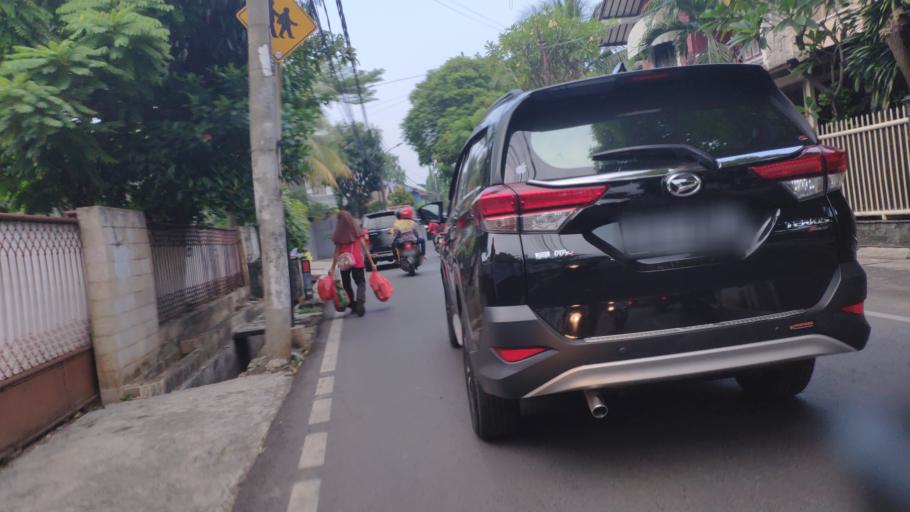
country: ID
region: West Java
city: Pamulang
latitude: -6.3046
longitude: 106.7988
